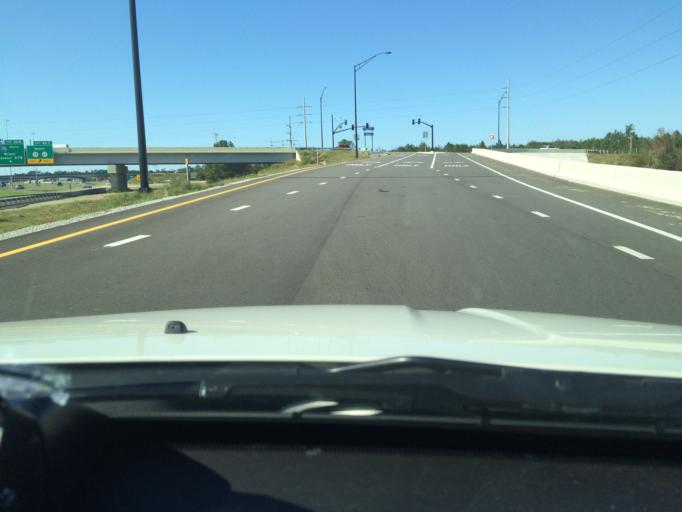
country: US
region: Mississippi
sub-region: Jackson County
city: Saint Martin
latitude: 30.4543
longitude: -88.8901
